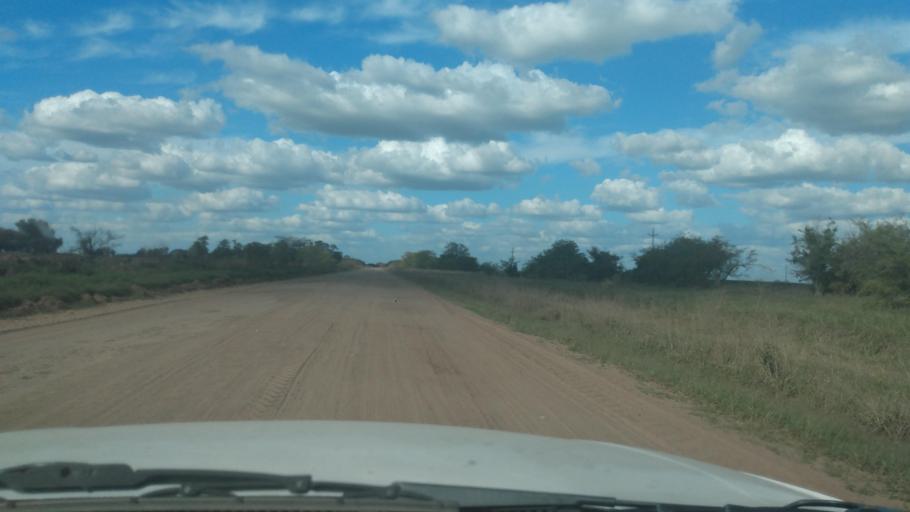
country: AR
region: Buenos Aires
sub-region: Partido de Navarro
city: Navarro
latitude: -35.0123
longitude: -59.4870
